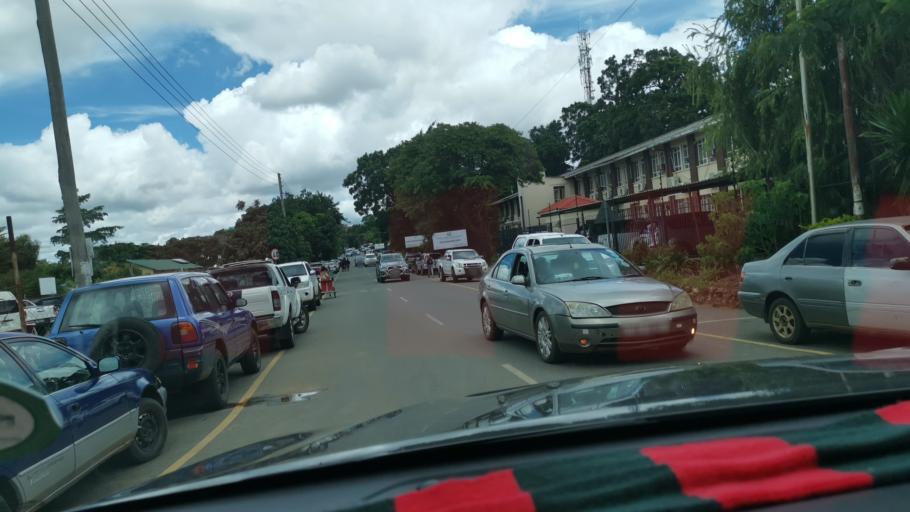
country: ZM
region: Lusaka
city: Lusaka
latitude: -15.4257
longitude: 28.3094
